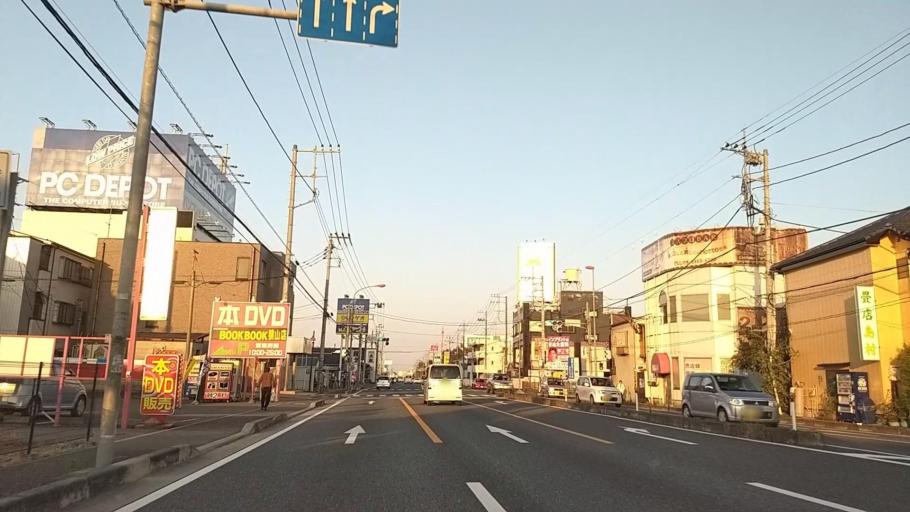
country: JP
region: Saitama
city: Sayama
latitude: 35.8763
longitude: 139.4300
